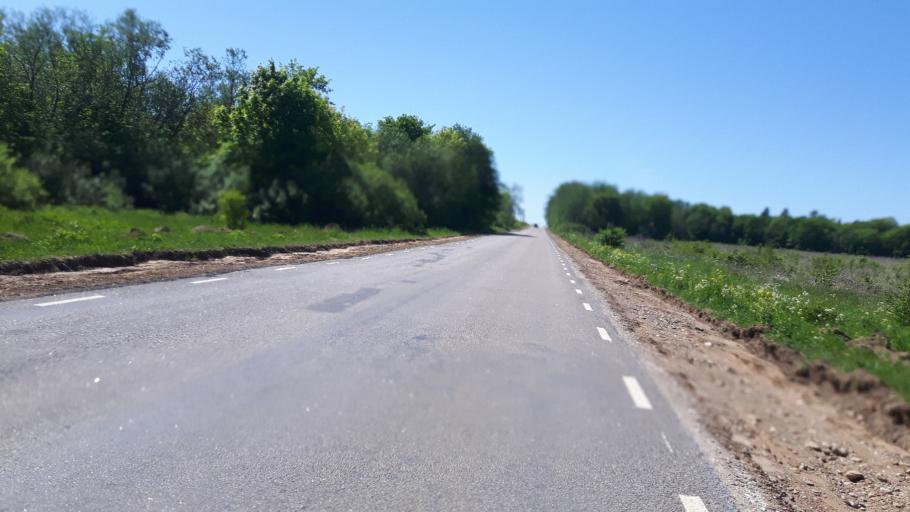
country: EE
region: Ida-Virumaa
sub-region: Narva-Joesuu linn
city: Narva-Joesuu
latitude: 59.4077
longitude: 27.9427
